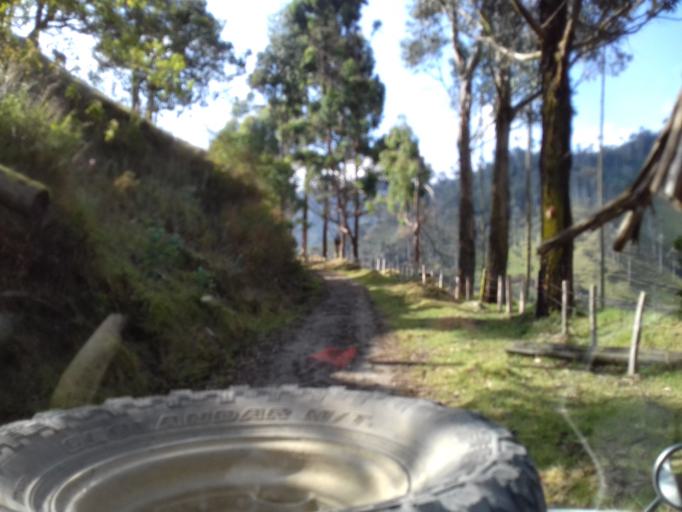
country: CO
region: Tolima
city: Cajamarca
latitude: 4.5321
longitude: -75.4657
